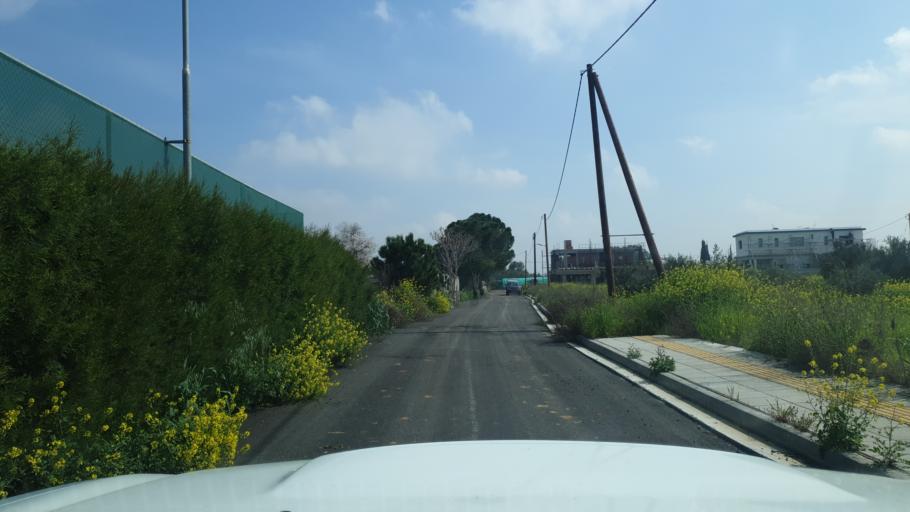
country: CY
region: Lefkosia
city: Kato Deftera
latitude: 35.0831
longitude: 33.2924
